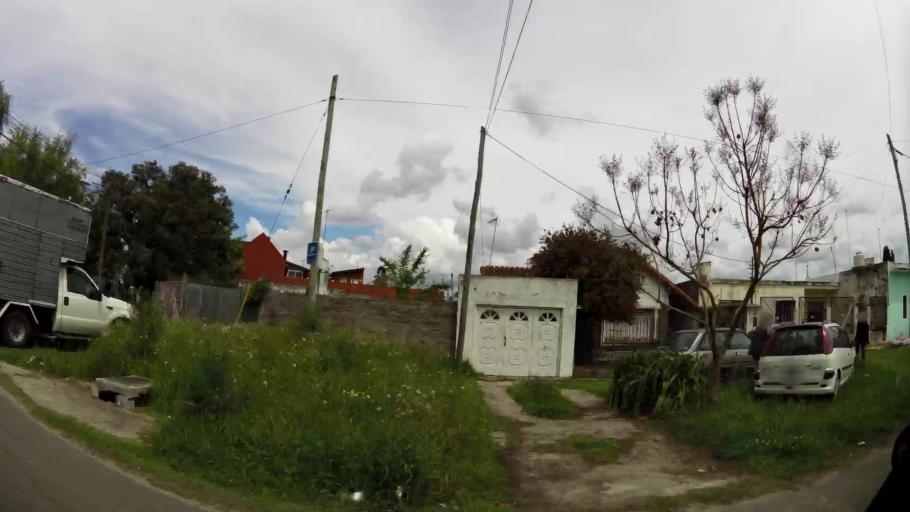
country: AR
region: Buenos Aires
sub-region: Partido de Quilmes
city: Quilmes
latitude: -34.7771
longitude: -58.2622
